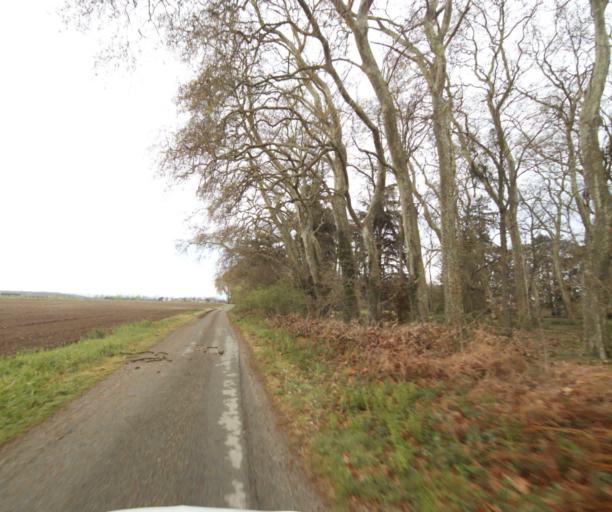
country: FR
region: Midi-Pyrenees
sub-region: Departement de l'Ariege
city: Mazeres
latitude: 43.2349
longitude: 1.6278
